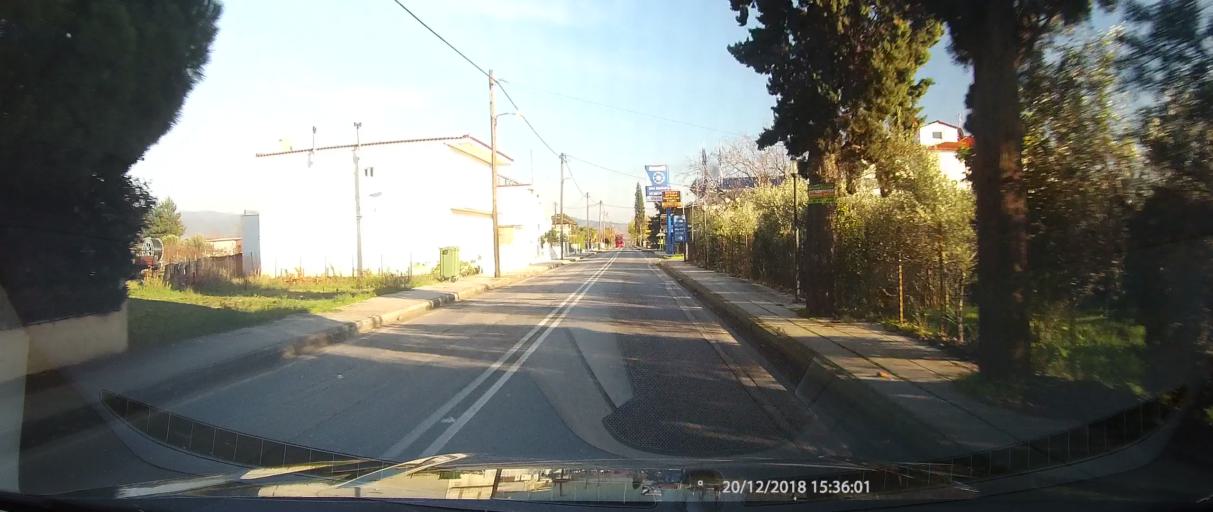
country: GR
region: Central Greece
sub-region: Nomos Fthiotidos
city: Lianokladhion
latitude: 38.9161
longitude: 22.3053
